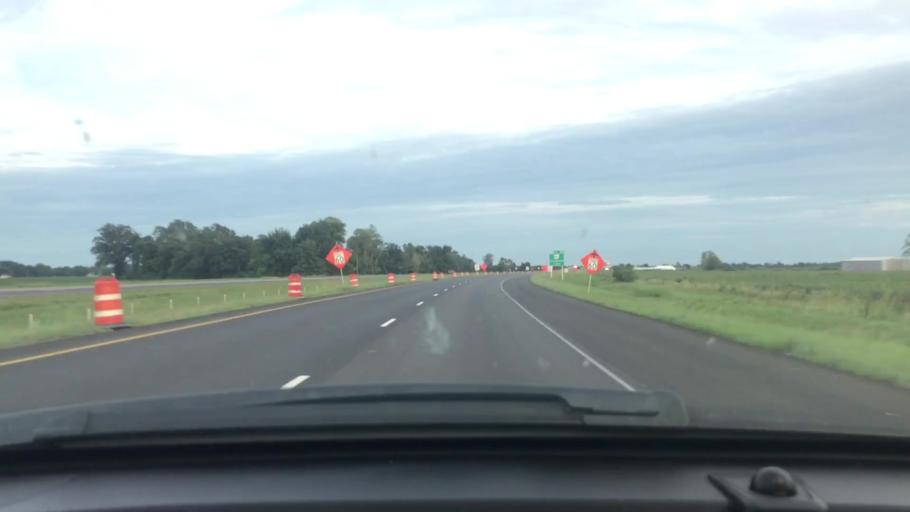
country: US
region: Arkansas
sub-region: Poinsett County
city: Trumann
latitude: 35.6435
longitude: -90.5127
